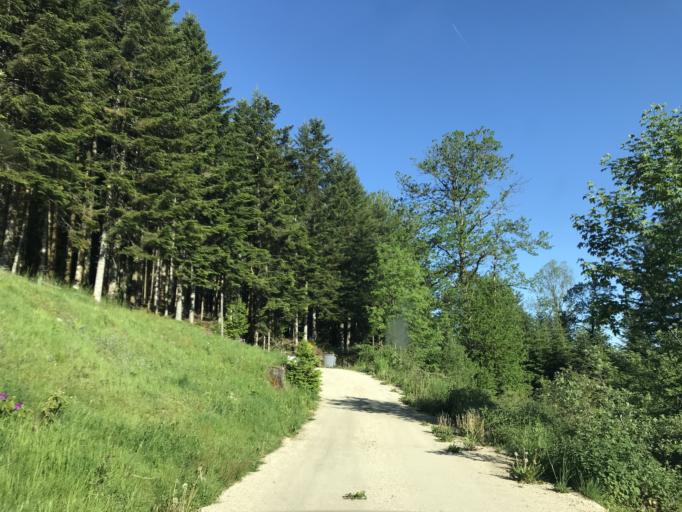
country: FR
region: Auvergne
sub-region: Departement du Puy-de-Dome
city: Job
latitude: 45.7050
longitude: 3.7086
